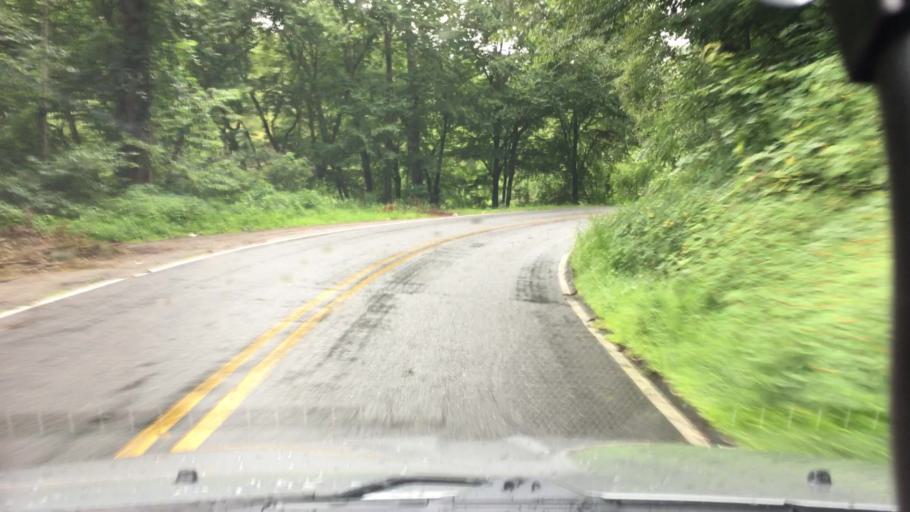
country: US
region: North Carolina
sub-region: Madison County
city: Mars Hill
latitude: 35.9104
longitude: -82.4726
